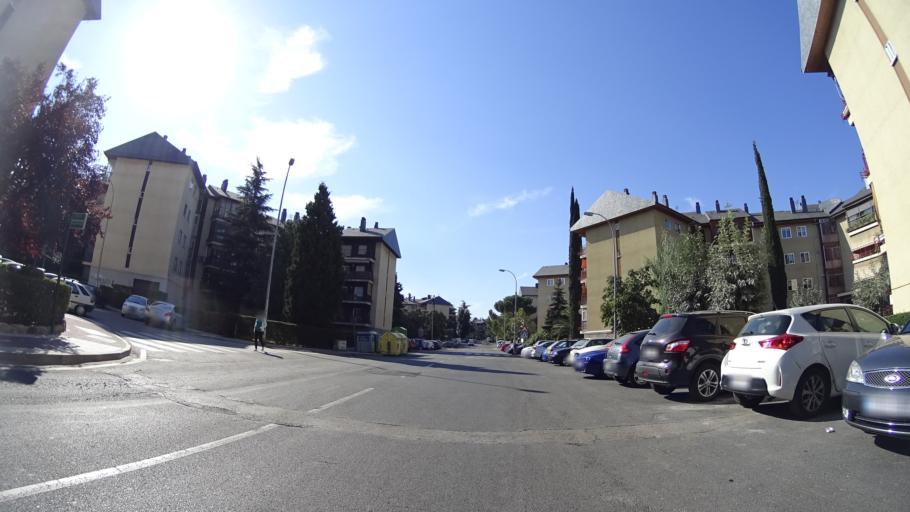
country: ES
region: Madrid
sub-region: Provincia de Madrid
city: Collado-Villalba
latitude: 40.6240
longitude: -4.0039
